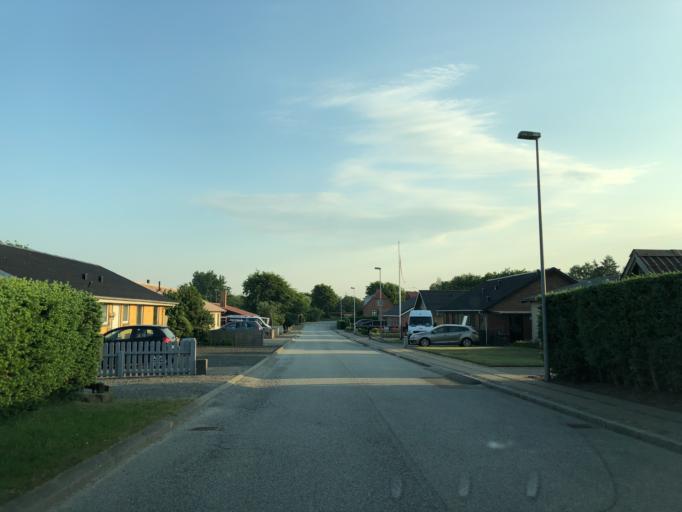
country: DK
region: Central Jutland
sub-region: Struer Kommune
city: Struer
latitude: 56.4172
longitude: 8.4905
